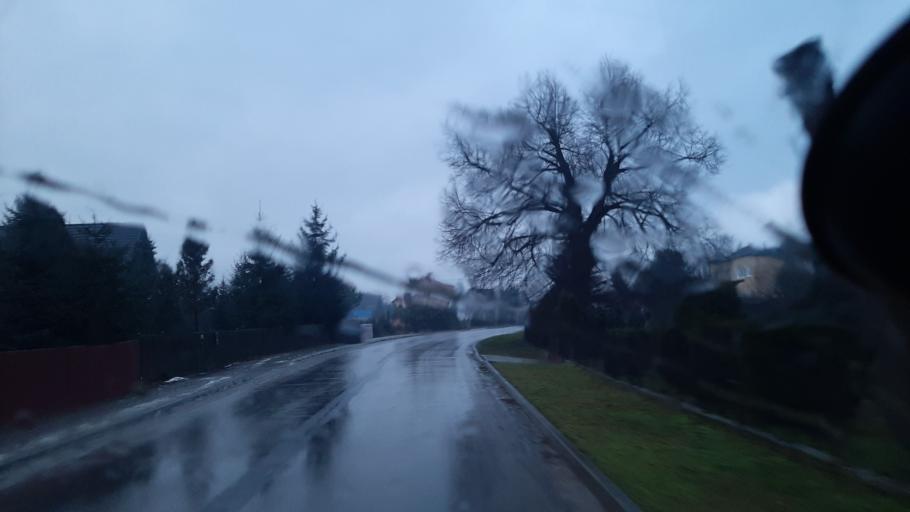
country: PL
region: Lublin Voivodeship
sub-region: Powiat lubartowski
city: Firlej
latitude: 51.5485
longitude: 22.5552
